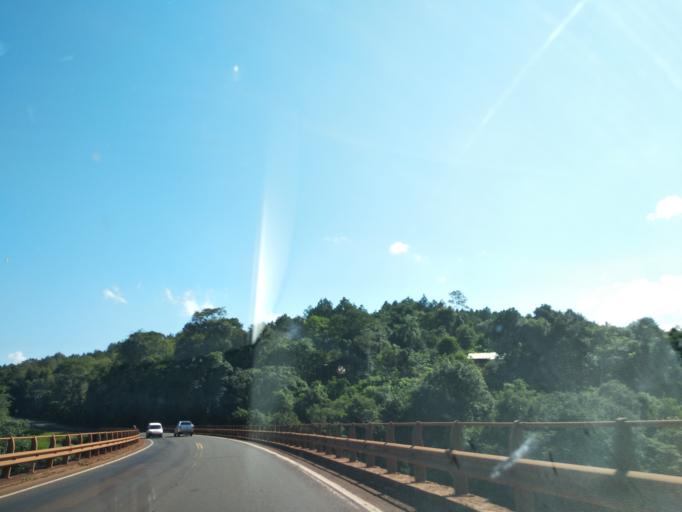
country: AR
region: Misiones
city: Puerto Piray
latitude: -26.4806
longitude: -54.6564
